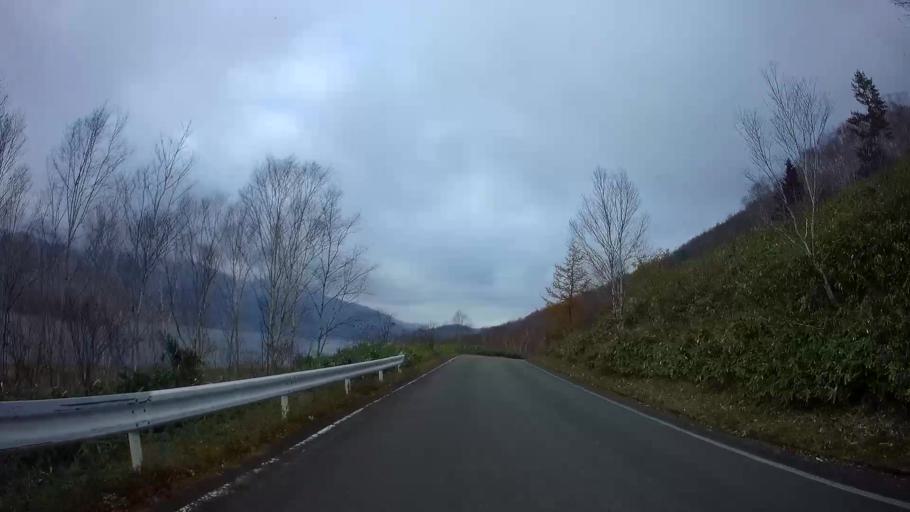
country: JP
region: Gunma
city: Nakanojomachi
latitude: 36.6967
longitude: 138.6561
